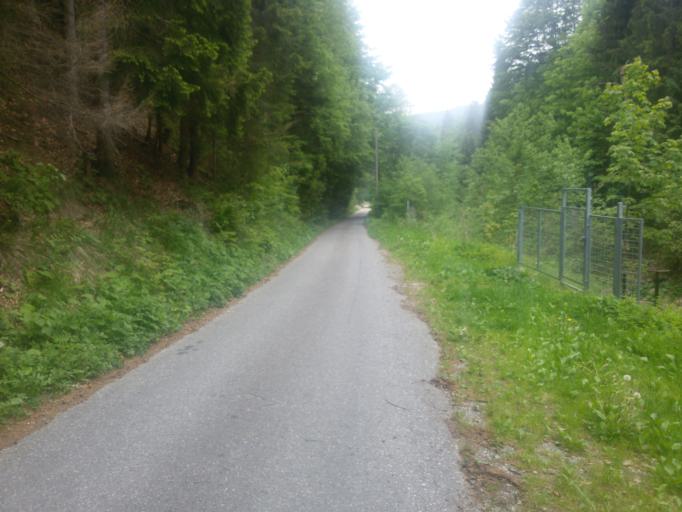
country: CZ
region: Olomoucky
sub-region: Okres Sumperk
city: Loucna nad Desnou
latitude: 50.1117
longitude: 17.1056
